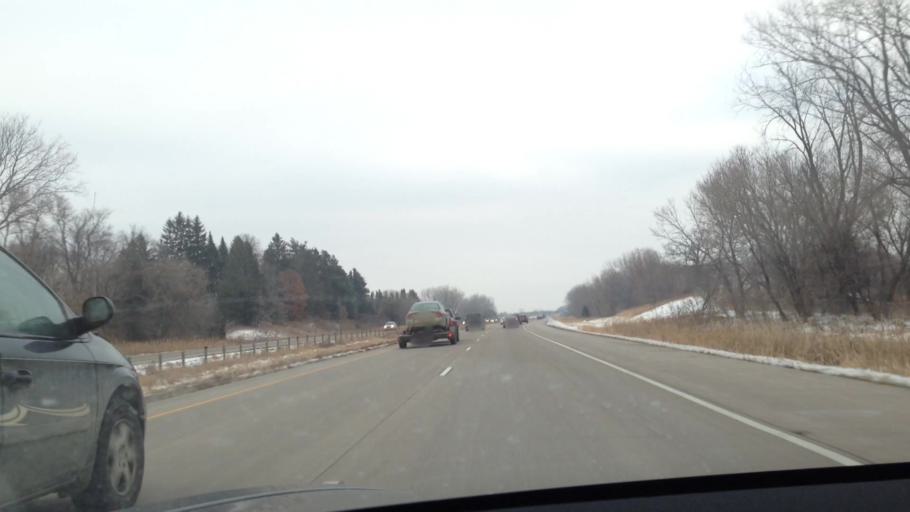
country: US
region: Minnesota
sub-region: Anoka County
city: Lino Lakes
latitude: 45.1881
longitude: -93.0887
